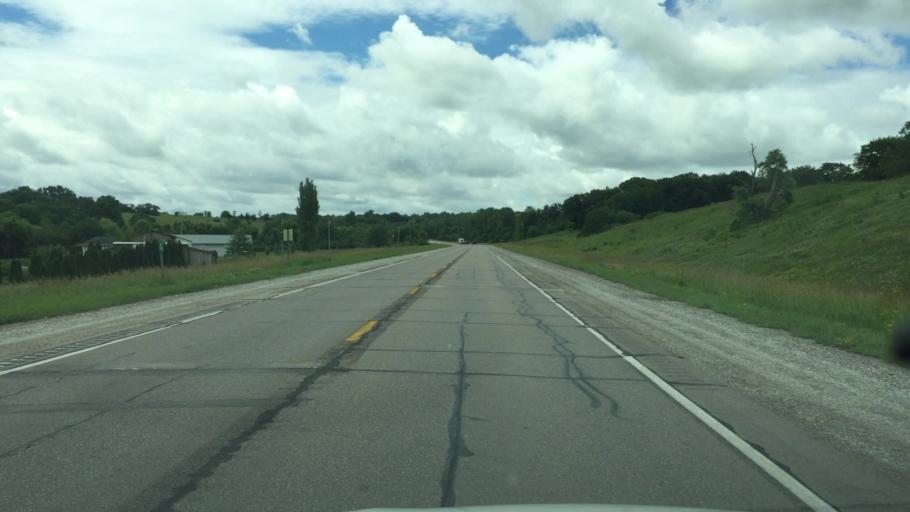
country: US
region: Iowa
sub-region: Jasper County
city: Monroe
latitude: 41.5402
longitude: -93.0997
